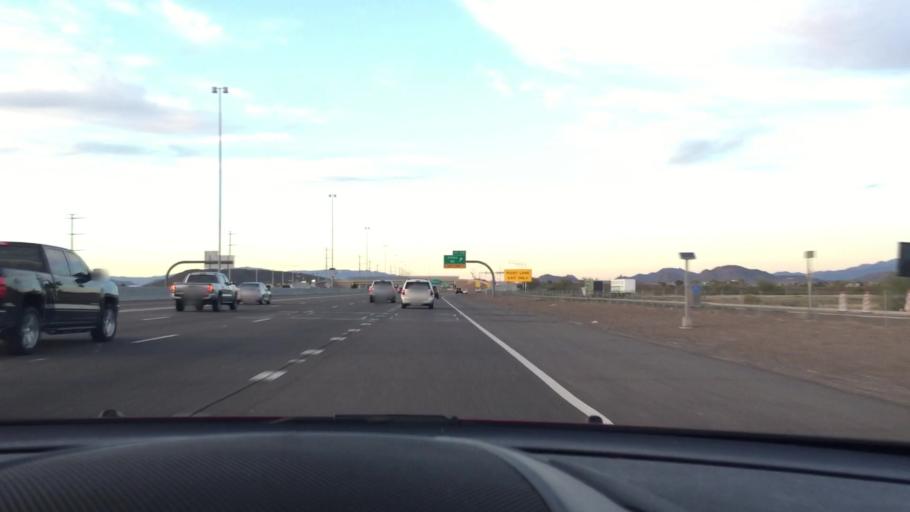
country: US
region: Arizona
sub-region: Maricopa County
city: Anthem
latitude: 33.7194
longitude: -112.1185
